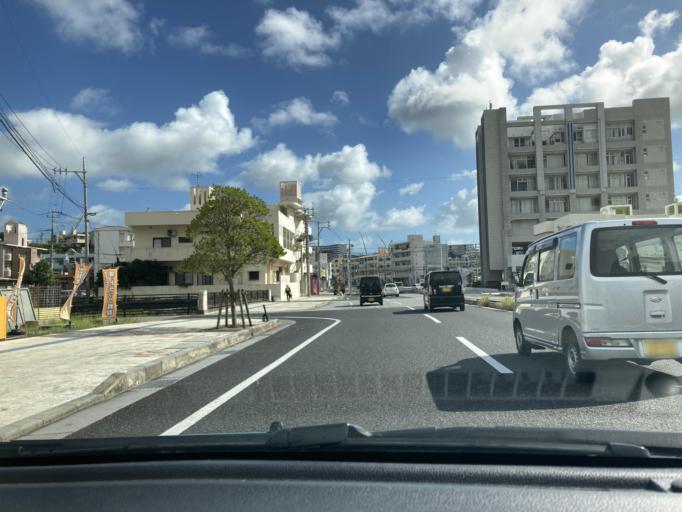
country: JP
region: Okinawa
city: Tomigusuku
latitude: 26.1970
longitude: 127.7269
